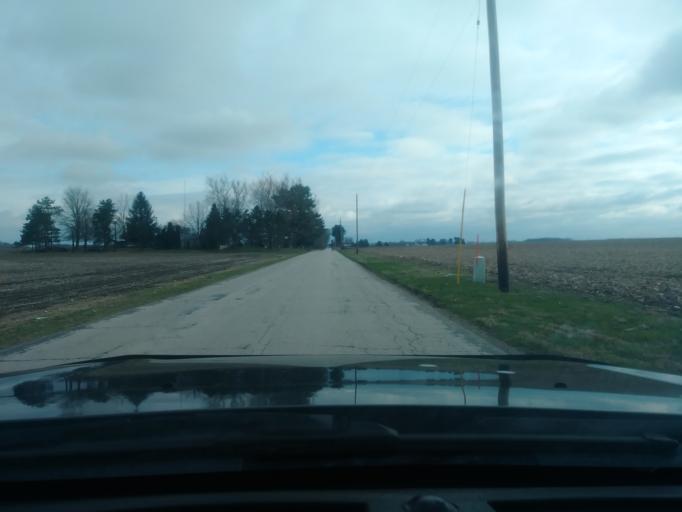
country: US
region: Indiana
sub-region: LaPorte County
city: LaPorte
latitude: 41.5791
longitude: -86.7980
